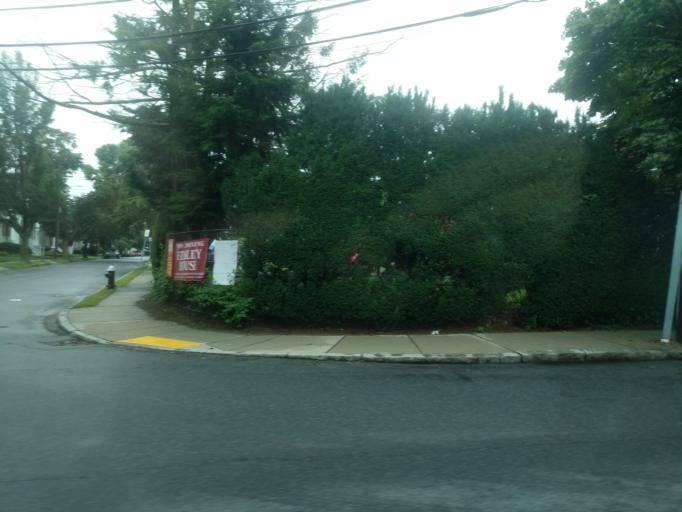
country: US
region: Massachusetts
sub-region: Middlesex County
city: Arlington
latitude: 42.4160
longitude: -71.1479
